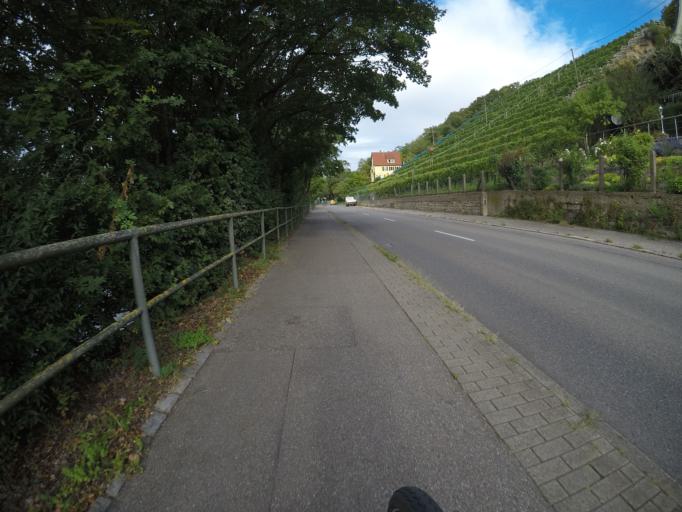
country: DE
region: Baden-Wuerttemberg
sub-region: Regierungsbezirk Stuttgart
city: Stuttgart Muehlhausen
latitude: 48.8260
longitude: 9.2208
